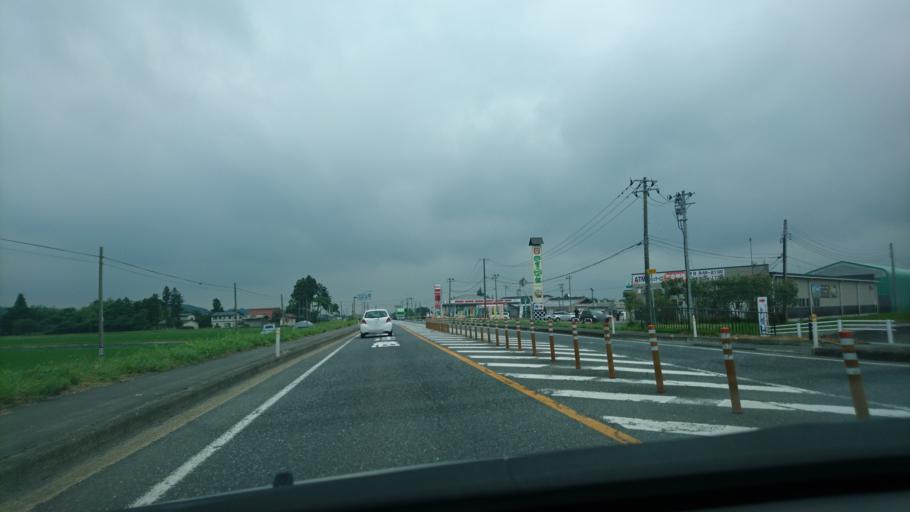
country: JP
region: Miyagi
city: Furukawa
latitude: 38.6683
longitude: 140.8679
